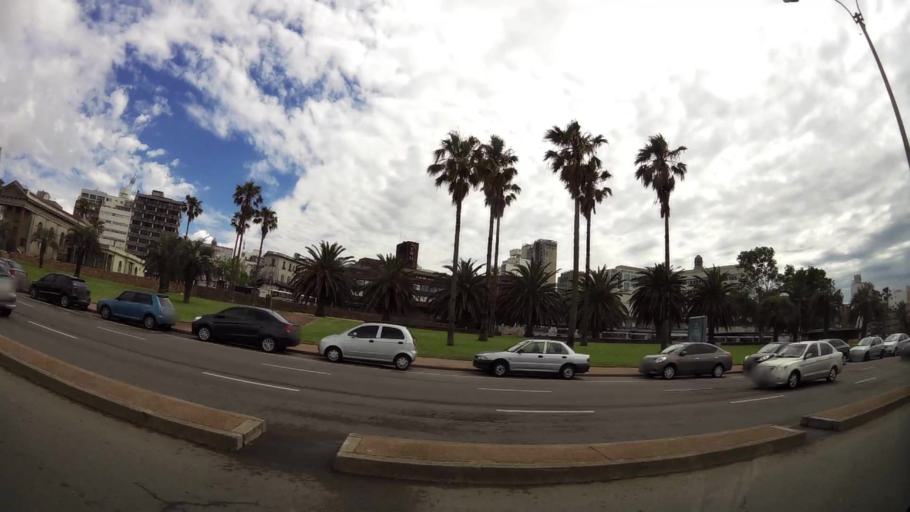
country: UY
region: Montevideo
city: Montevideo
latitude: -34.9102
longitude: -56.2026
